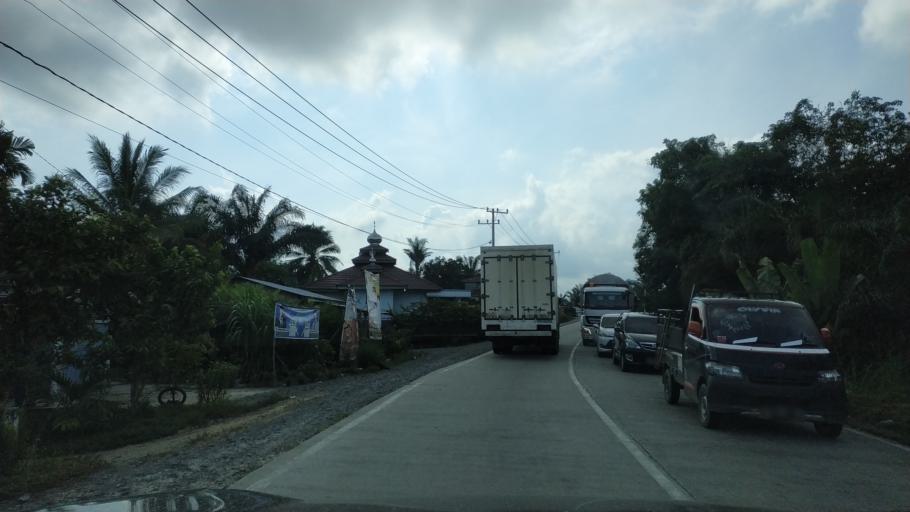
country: ID
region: Riau
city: Pangkalan Kasai
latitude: -0.6968
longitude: 102.4885
